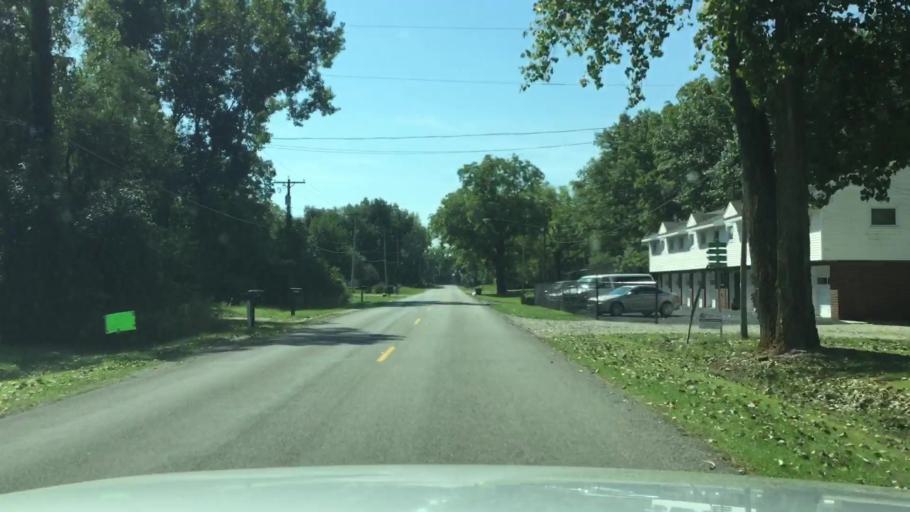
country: US
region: Michigan
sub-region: Lenawee County
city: Manitou Beach-Devils Lake
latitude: 41.9877
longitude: -84.2807
